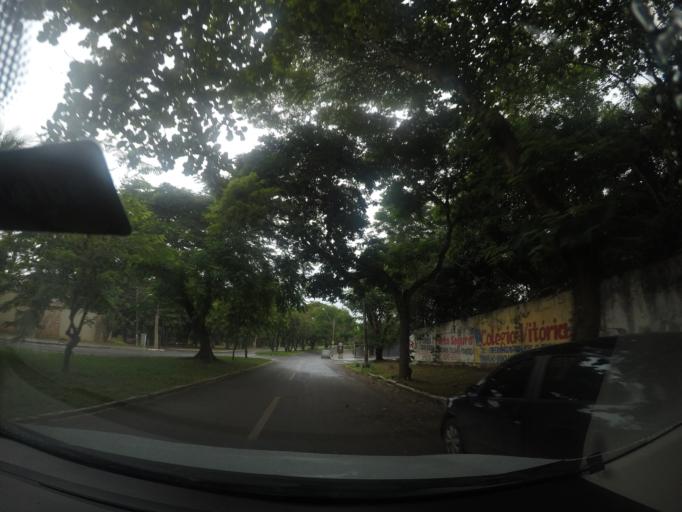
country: BR
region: Goias
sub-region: Goiania
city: Goiania
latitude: -16.6510
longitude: -49.2295
